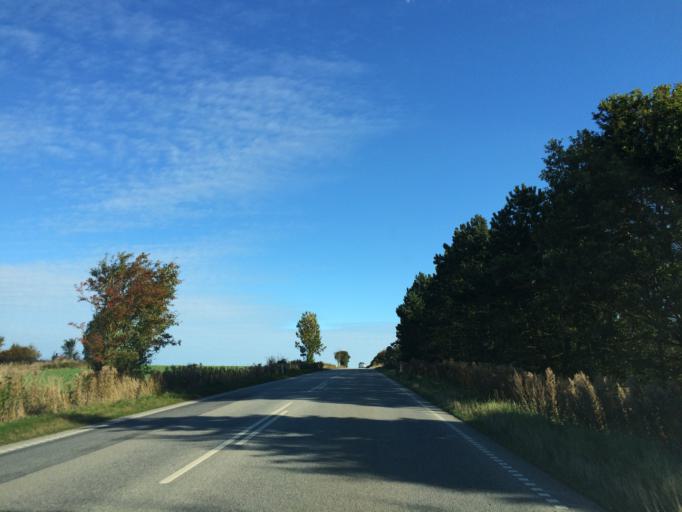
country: DK
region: Central Jutland
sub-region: Randers Kommune
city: Randers
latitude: 56.4176
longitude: 10.0181
